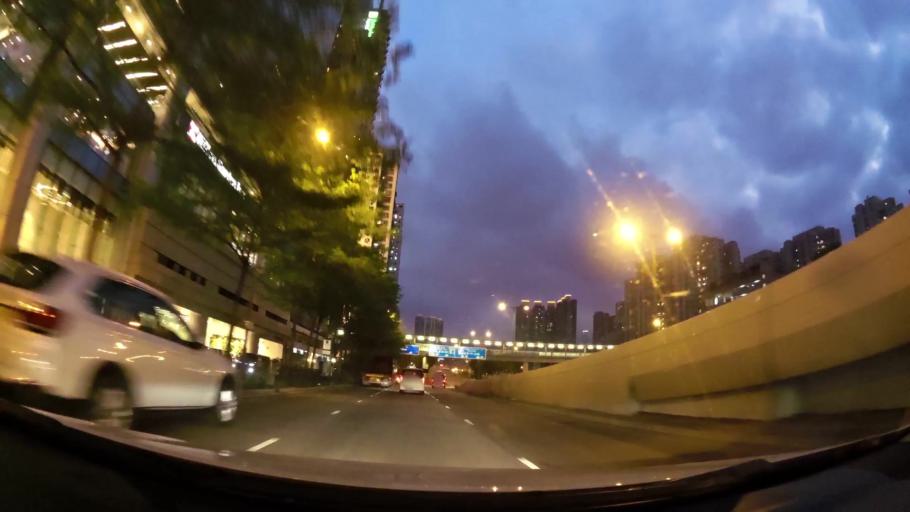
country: HK
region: Sham Shui Po
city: Sham Shui Po
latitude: 22.3161
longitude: 114.1668
